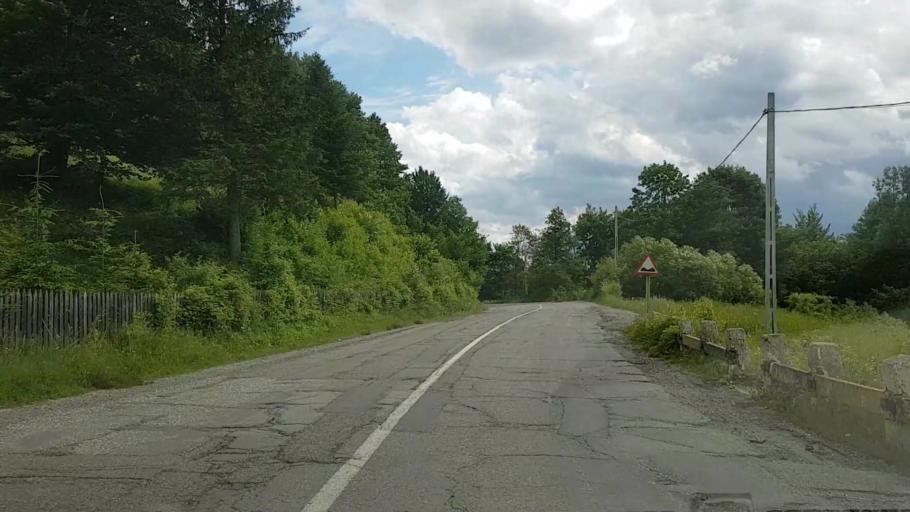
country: RO
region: Neamt
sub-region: Comuna Bicaz
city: Dodeni
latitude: 46.9896
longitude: 26.1023
